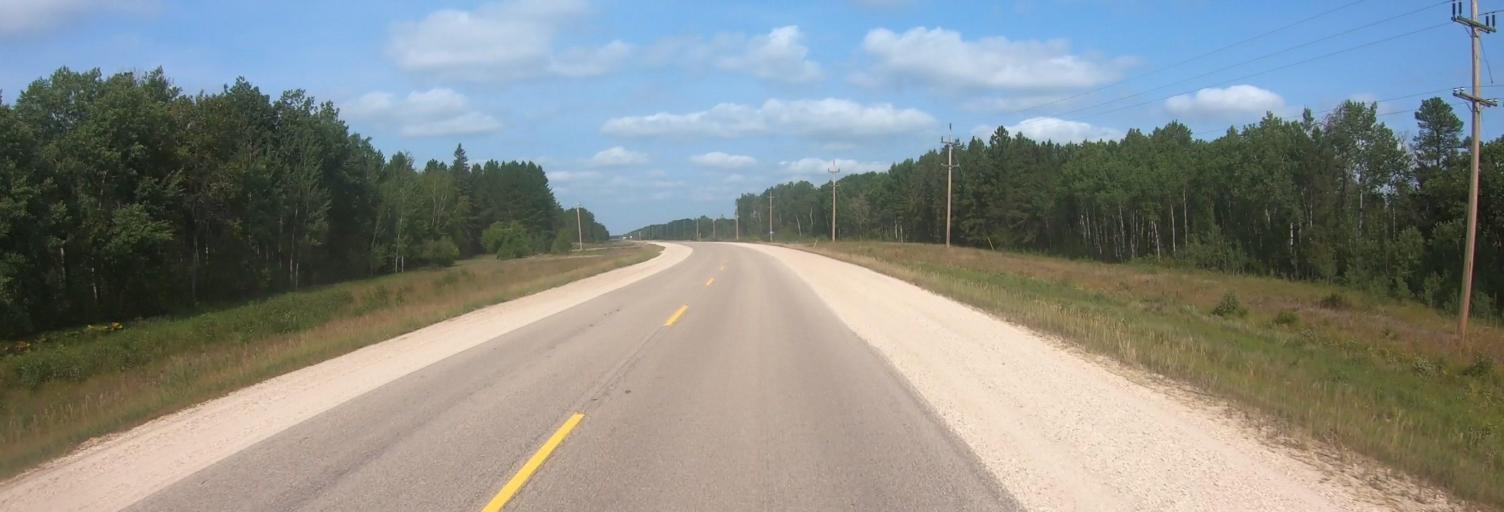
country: CA
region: Manitoba
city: La Broquerie
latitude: 49.2179
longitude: -96.3024
